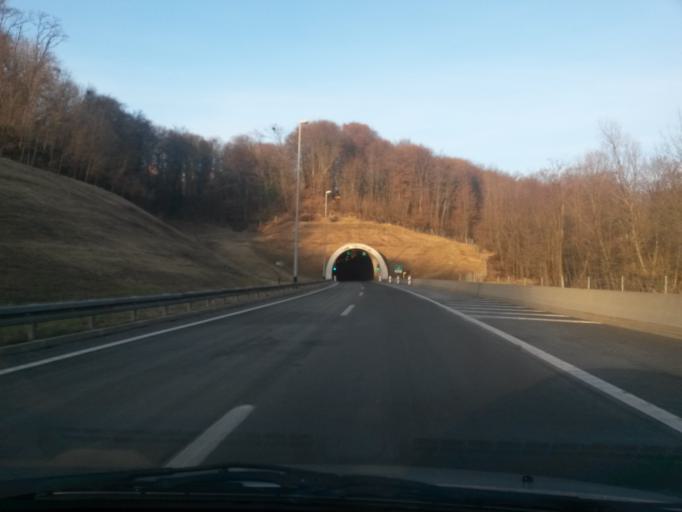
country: HR
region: Varazdinska
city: Ljubescica
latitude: 46.2196
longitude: 16.4068
